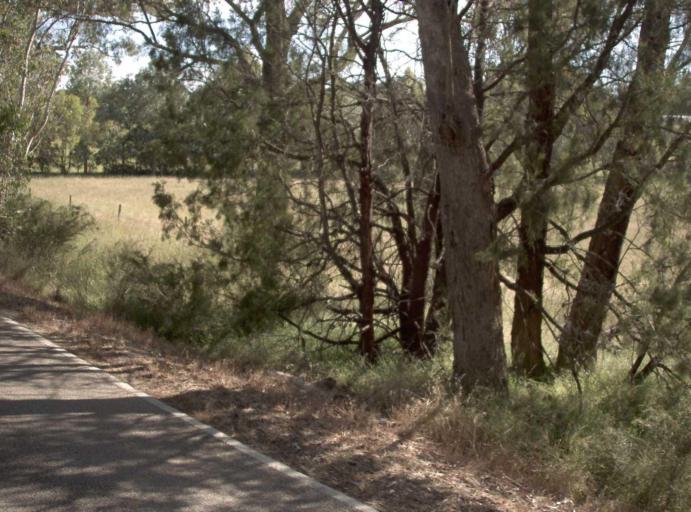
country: AU
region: Victoria
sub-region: East Gippsland
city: Lakes Entrance
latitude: -37.7528
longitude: 147.8147
